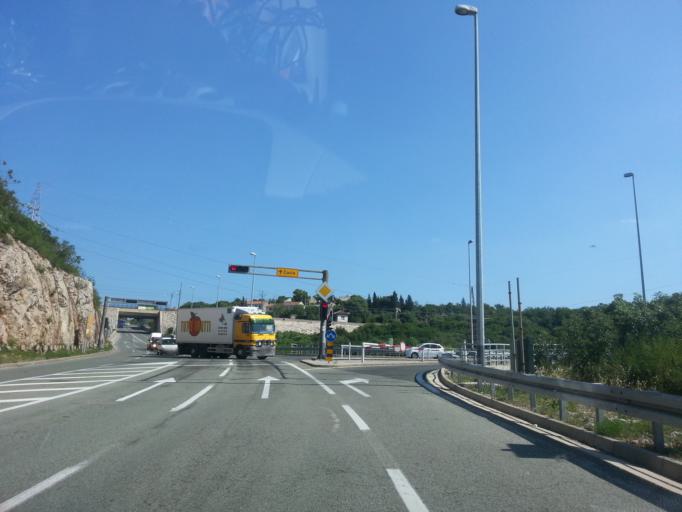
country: HR
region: Primorsko-Goranska
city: Bakar
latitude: 45.3122
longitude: 14.5281
